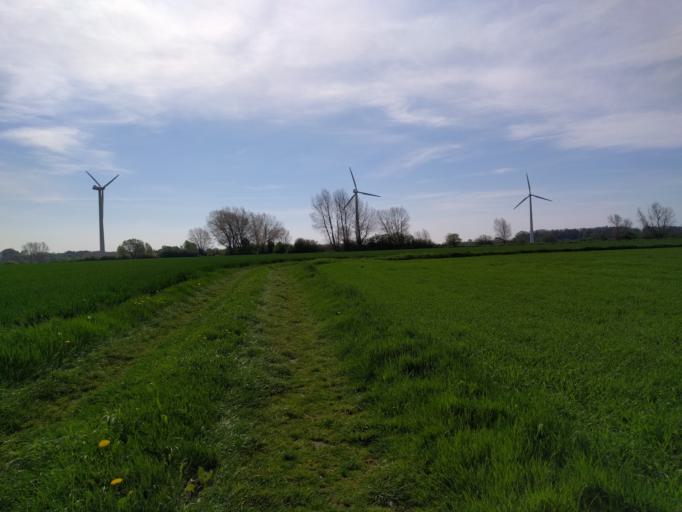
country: DK
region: South Denmark
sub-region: Odense Kommune
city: Bullerup
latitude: 55.4002
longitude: 10.5292
